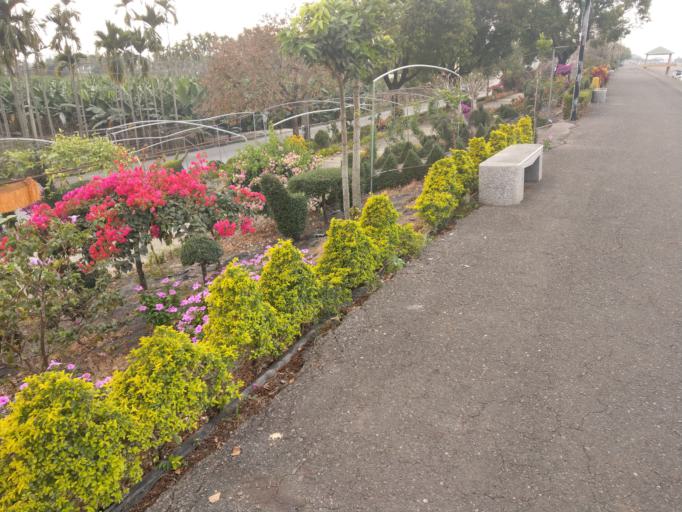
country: TW
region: Taiwan
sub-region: Pingtung
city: Pingtung
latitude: 22.7833
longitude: 120.5362
